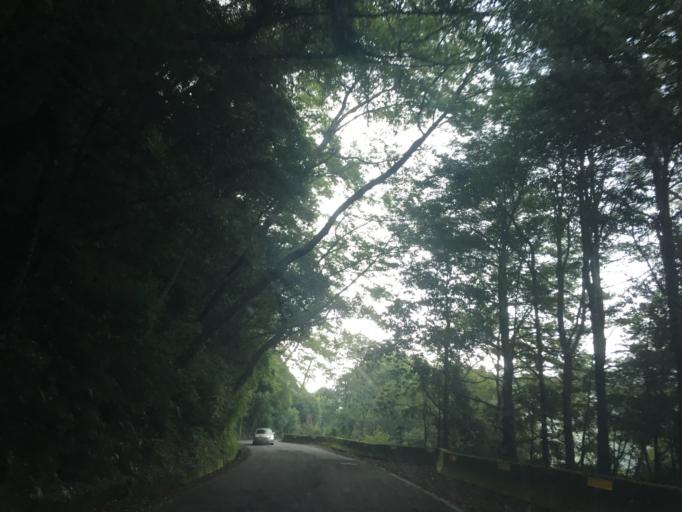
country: TW
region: Taiwan
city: Fengyuan
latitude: 24.2403
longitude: 120.9798
